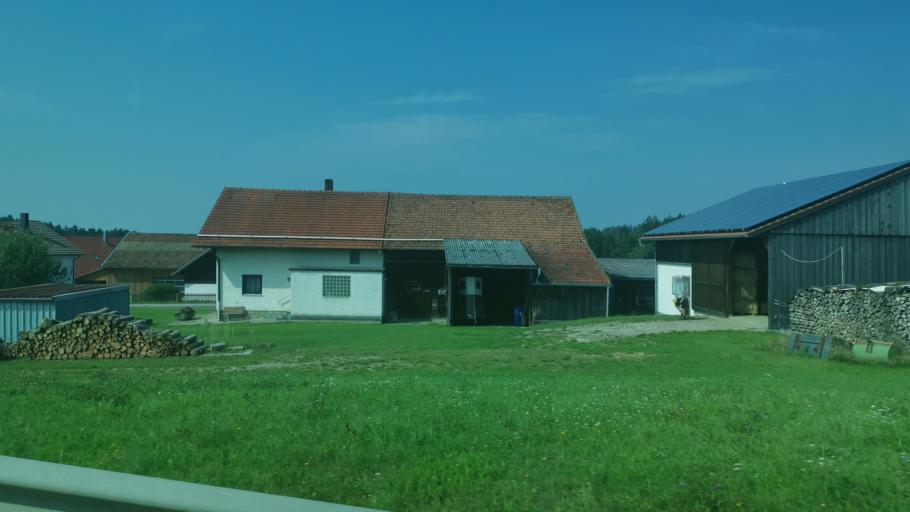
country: DE
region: Bavaria
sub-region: Upper Palatinate
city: Pemfling
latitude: 49.2707
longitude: 12.6308
